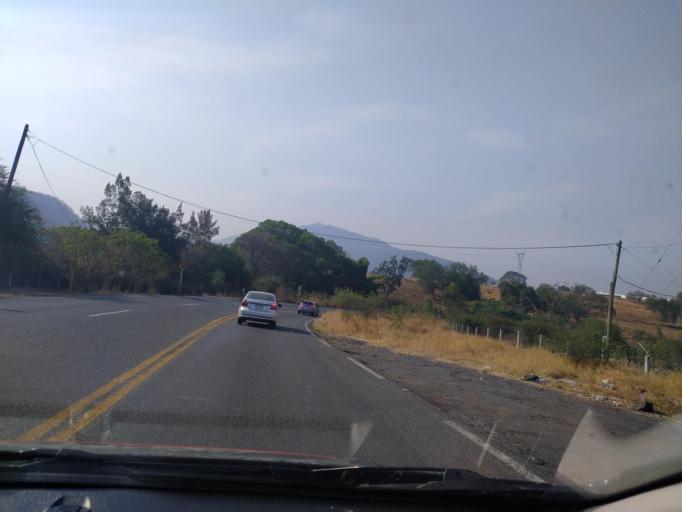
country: MX
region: Jalisco
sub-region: Acatlan de Juarez
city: Villa de los Ninos
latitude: 20.4181
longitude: -103.5794
